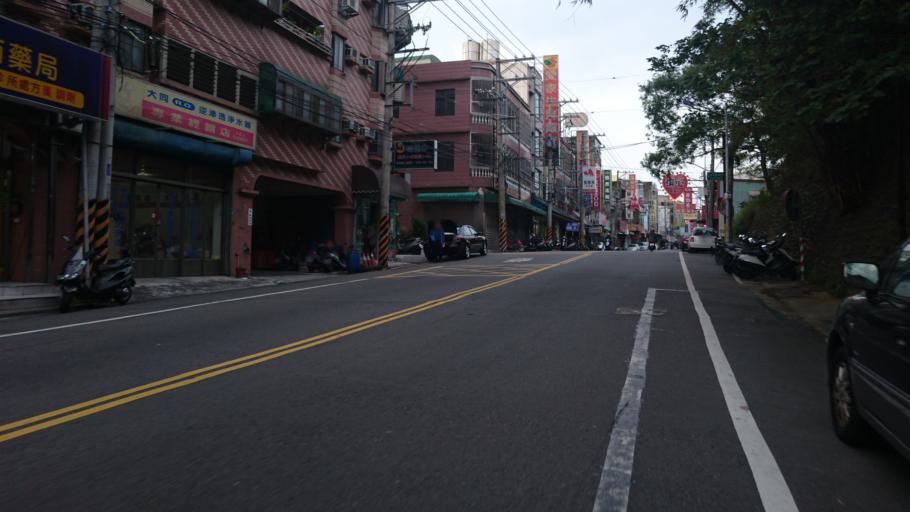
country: TW
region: Taiwan
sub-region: Hsinchu
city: Hsinchu
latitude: 24.7839
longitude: 120.9676
